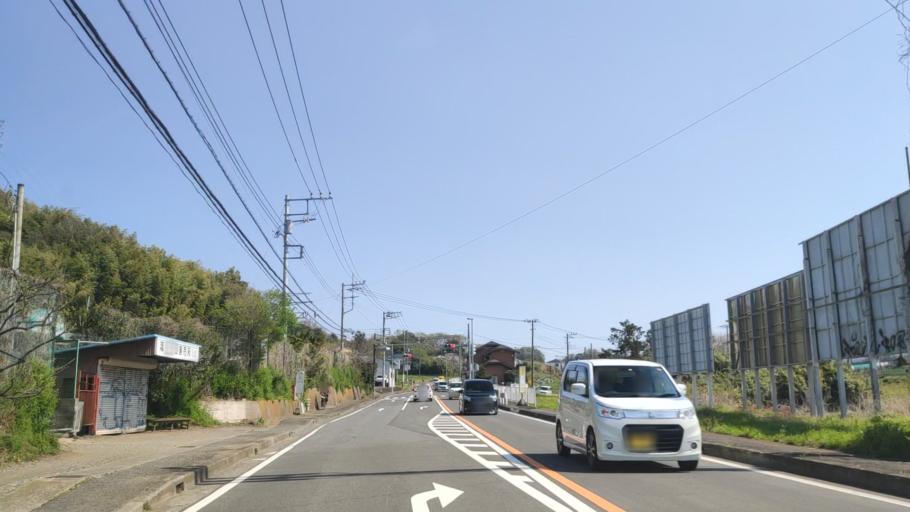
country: JP
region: Kanagawa
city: Oiso
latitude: 35.3268
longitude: 139.2894
